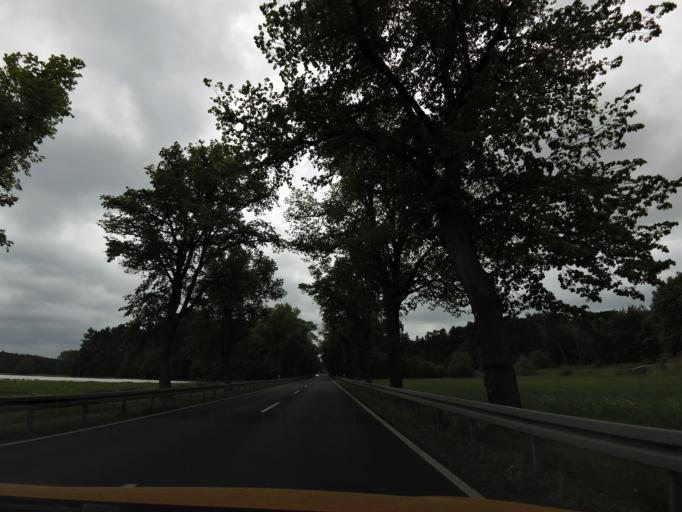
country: DE
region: Brandenburg
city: Beelitz
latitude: 52.1932
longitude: 12.9515
